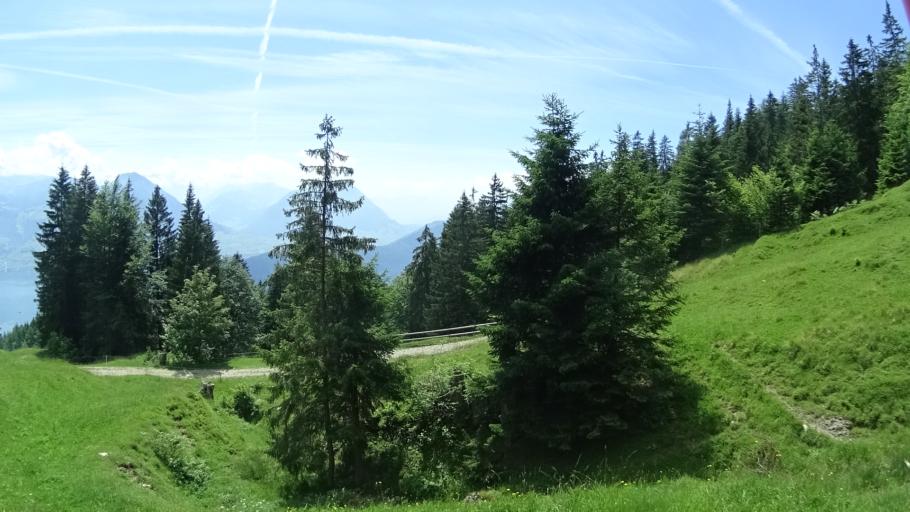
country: CH
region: Lucerne
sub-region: Lucerne-Land District
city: Vitznau
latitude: 47.0377
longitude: 8.4743
